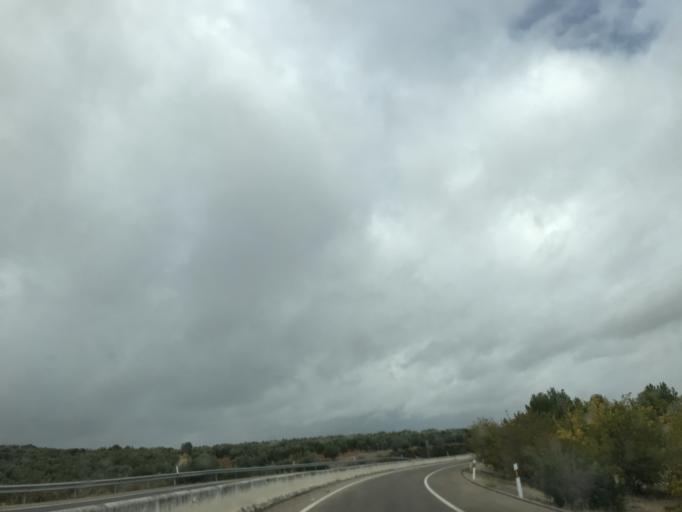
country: ES
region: Andalusia
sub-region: Provincia de Jaen
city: Bailen
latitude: 38.1221
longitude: -3.7618
